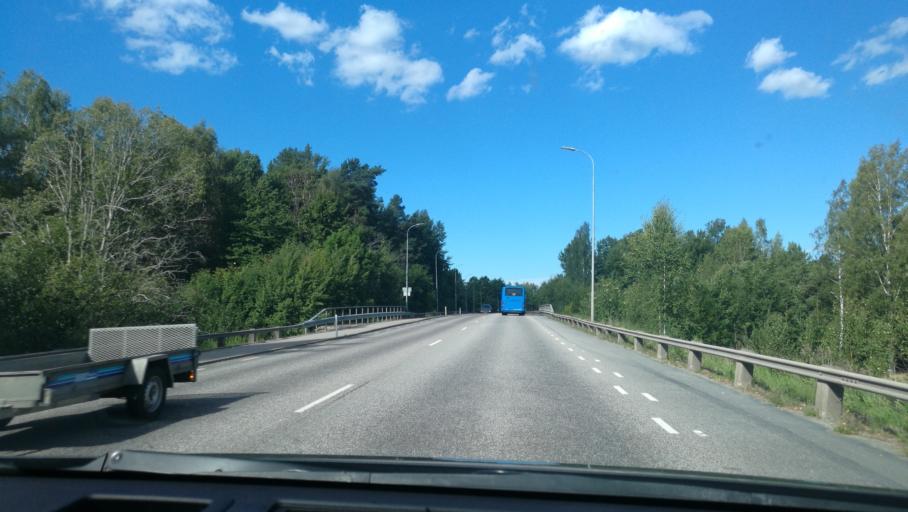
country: SE
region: Vaestra Goetaland
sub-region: Mariestads Kommun
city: Mariestad
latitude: 58.6900
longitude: 13.8182
